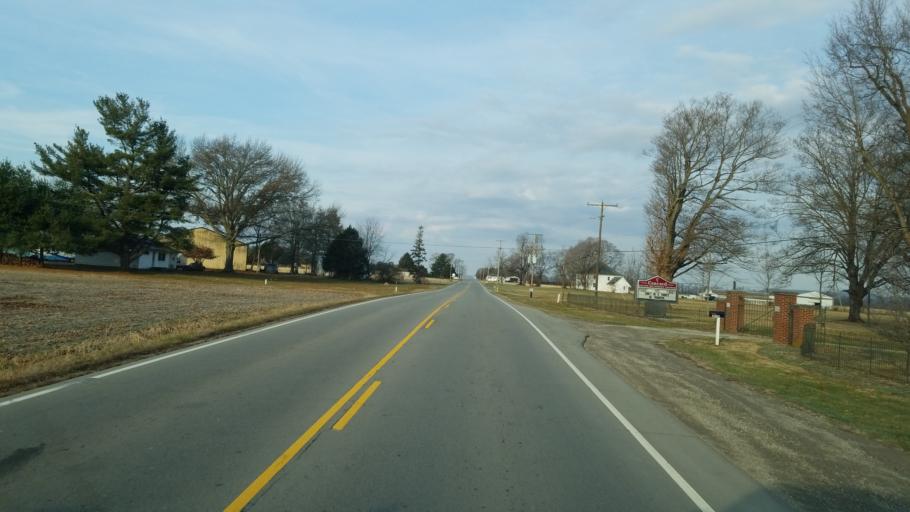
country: US
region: Ohio
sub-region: Ross County
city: Chillicothe
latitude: 39.2901
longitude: -82.8748
